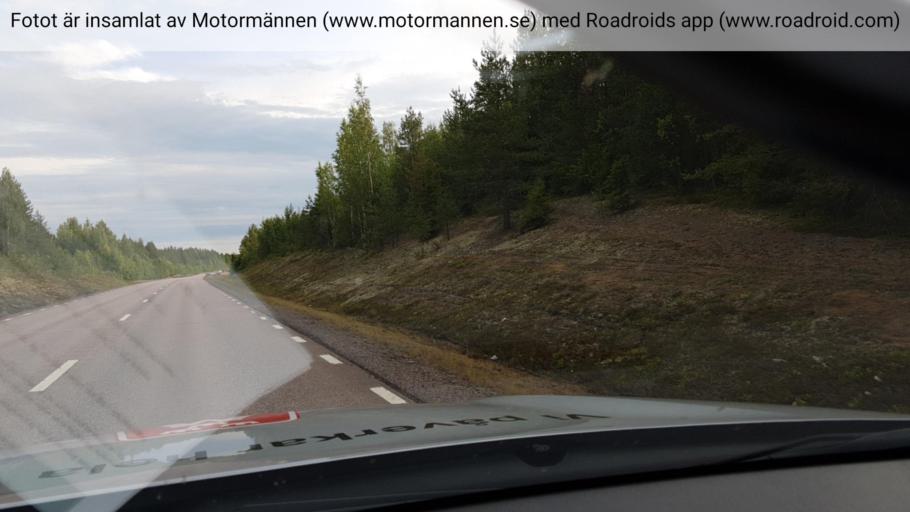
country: SE
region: Norrbotten
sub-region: Kalix Kommun
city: Toere
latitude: 65.9872
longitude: 22.6944
